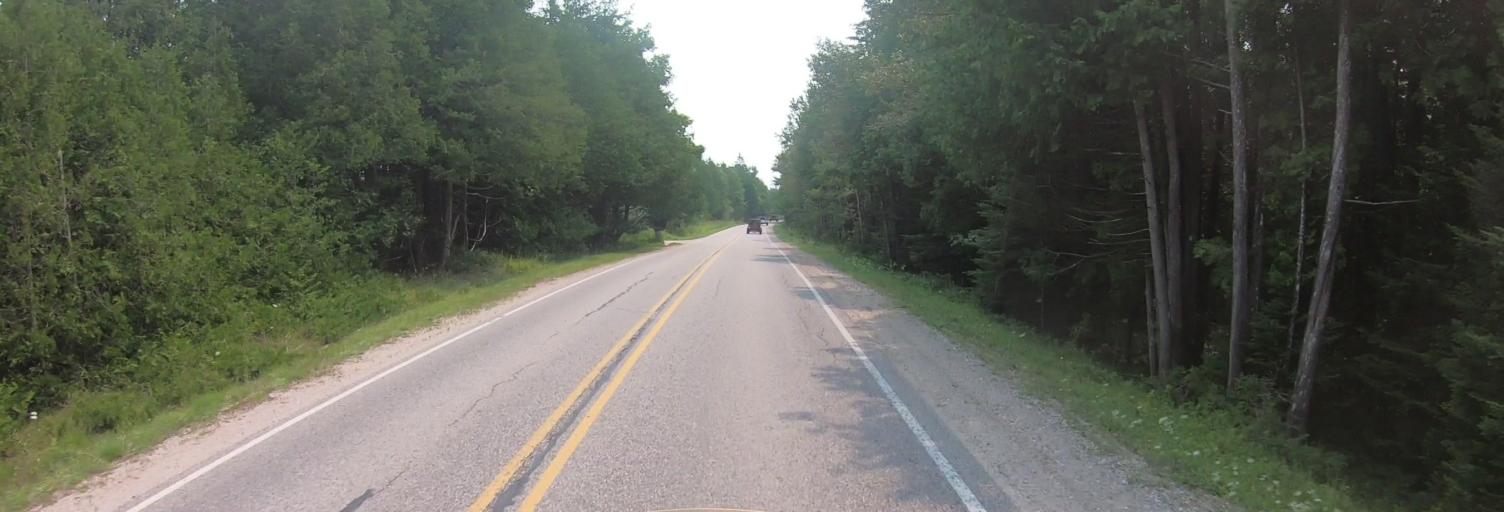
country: CA
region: Ontario
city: Thessalon
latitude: 45.9933
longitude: -83.7023
